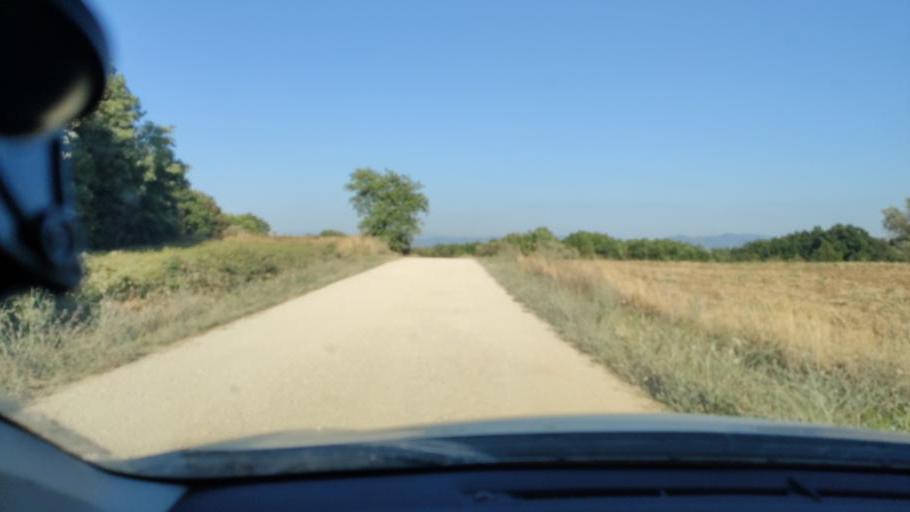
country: IT
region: Umbria
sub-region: Provincia di Terni
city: Amelia
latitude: 42.5389
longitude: 12.3762
